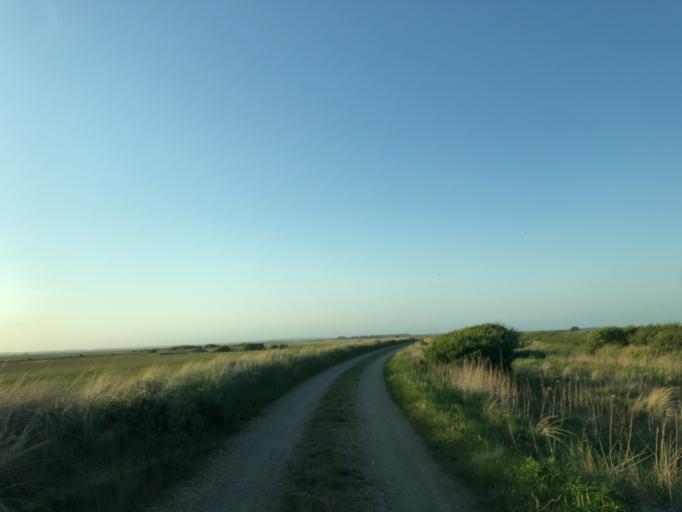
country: DK
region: Central Jutland
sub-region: Ringkobing-Skjern Kommune
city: Ringkobing
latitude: 56.2116
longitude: 8.1633
